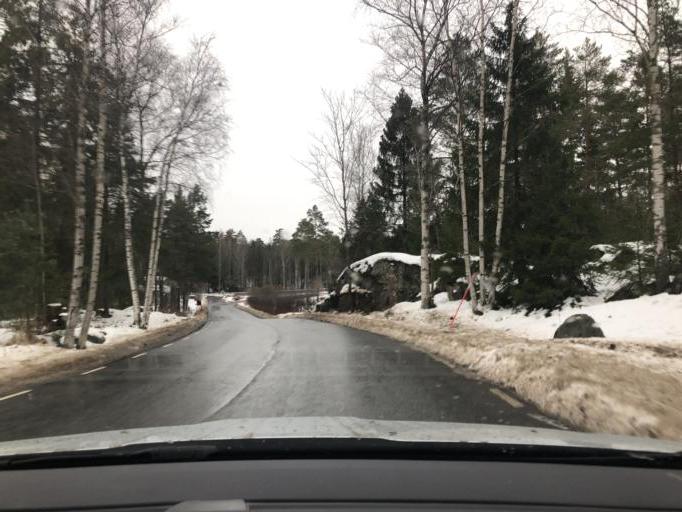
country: SE
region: Stockholm
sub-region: Botkyrka Kommun
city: Tullinge
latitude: 59.2346
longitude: 17.8926
